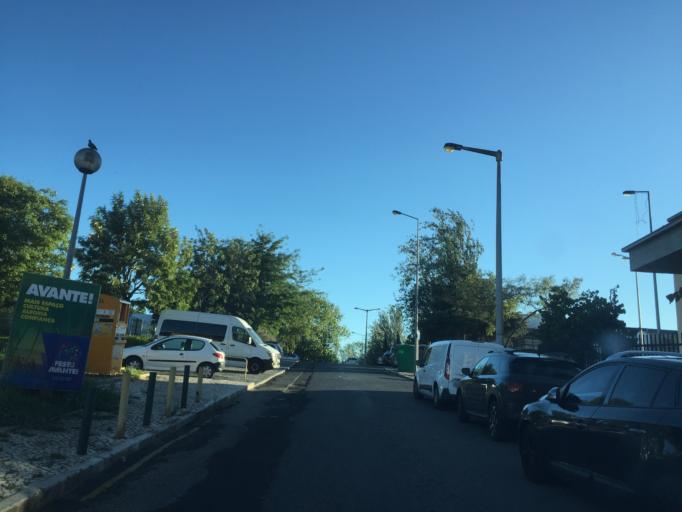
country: PT
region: Lisbon
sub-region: Odivelas
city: Povoa de Santo Adriao
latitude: 38.8019
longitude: -9.1638
